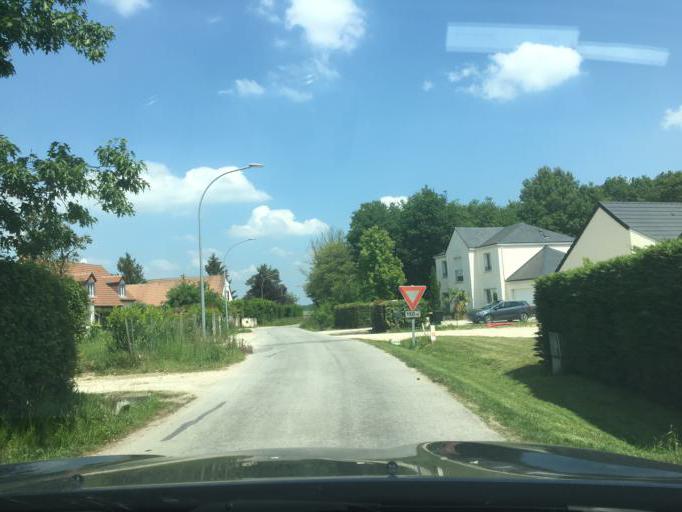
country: FR
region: Centre
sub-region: Departement du Loiret
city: Trainou
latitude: 47.9743
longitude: 2.1131
